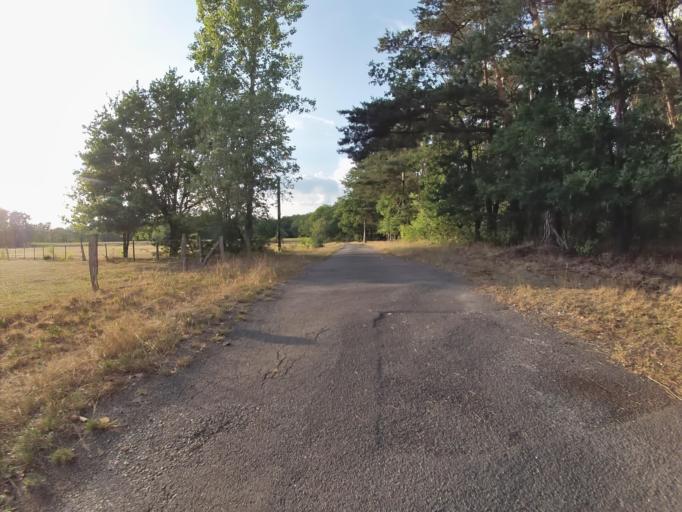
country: DE
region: North Rhine-Westphalia
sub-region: Regierungsbezirk Munster
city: Westerkappeln
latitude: 52.3651
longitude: 7.8940
